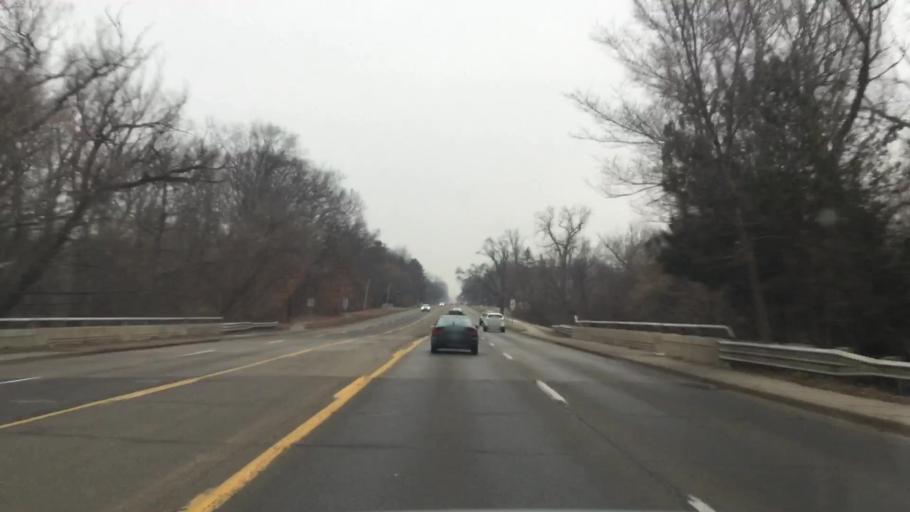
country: US
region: Michigan
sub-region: Wayne County
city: Livonia
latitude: 42.4056
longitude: -83.3544
